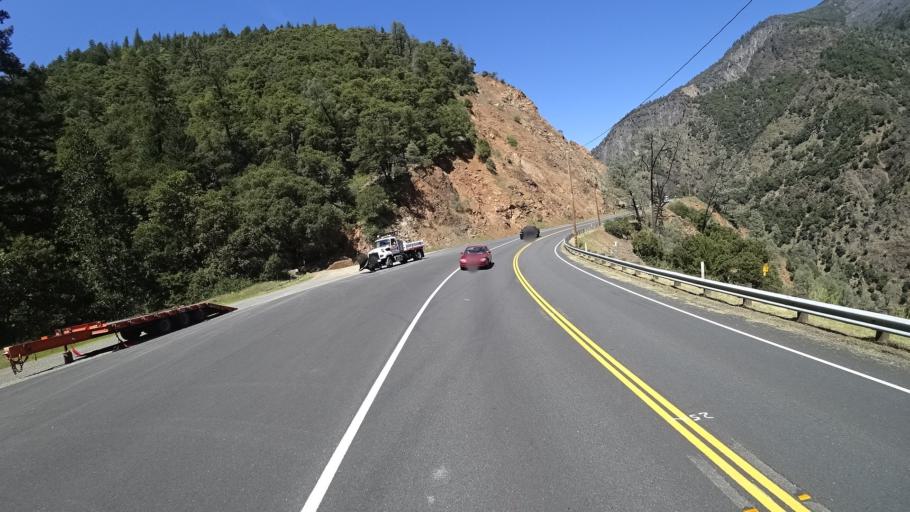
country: US
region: California
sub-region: Humboldt County
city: Willow Creek
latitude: 40.8130
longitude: -123.4789
